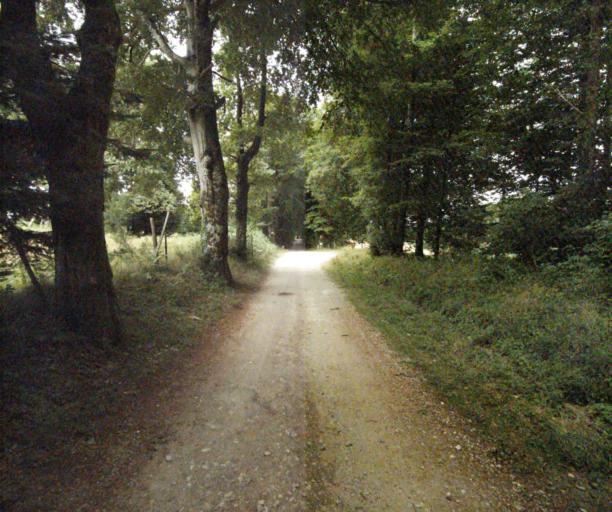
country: FR
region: Midi-Pyrenees
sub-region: Departement du Tarn
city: Soreze
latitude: 43.4214
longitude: 2.1039
